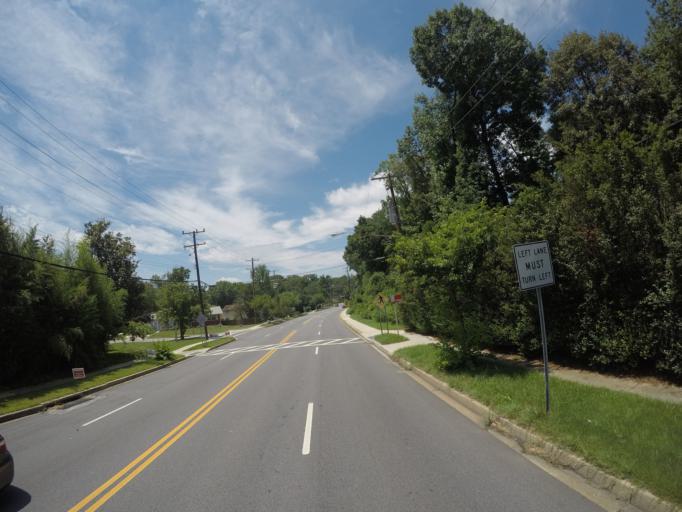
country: US
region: Maryland
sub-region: Prince George's County
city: New Carrollton
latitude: 38.9726
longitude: -76.8911
